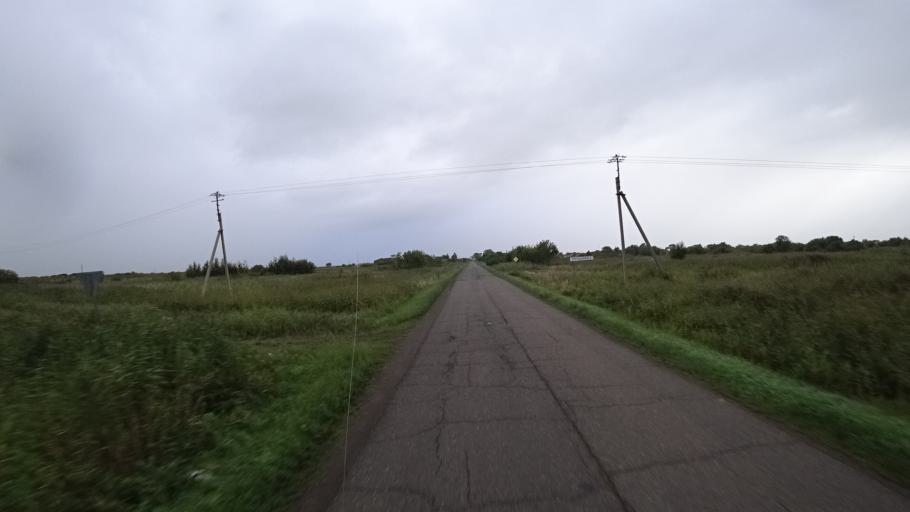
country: RU
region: Primorskiy
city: Chernigovka
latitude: 44.3940
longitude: 132.5284
